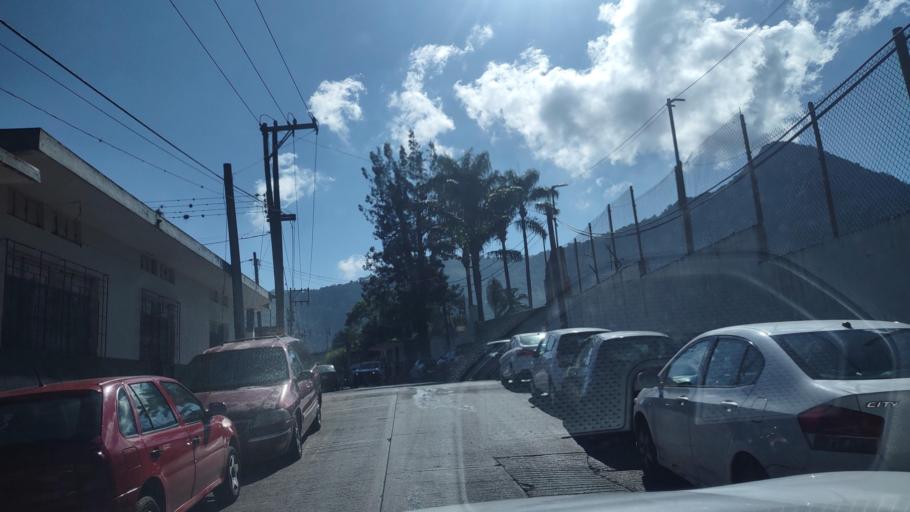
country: MX
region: Veracruz
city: Cuautlapan
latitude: 18.8735
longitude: -97.0237
